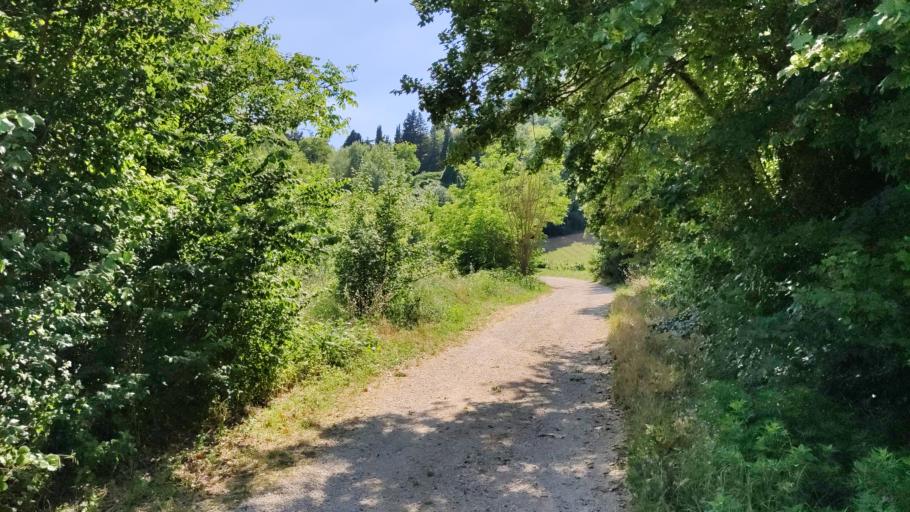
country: IT
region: Umbria
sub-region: Provincia di Terni
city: Amelia
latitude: 42.5584
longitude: 12.4198
